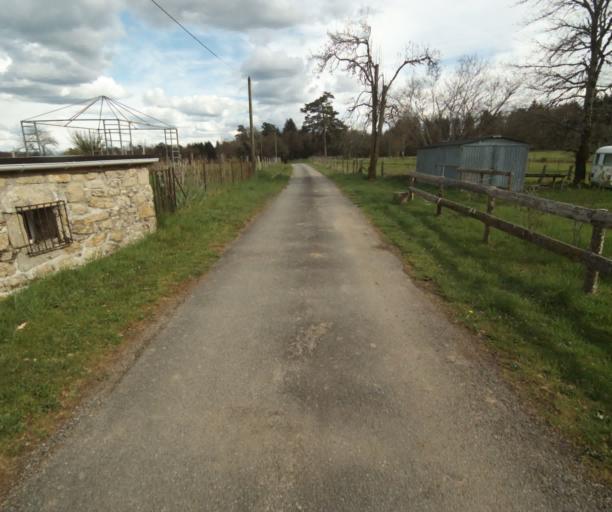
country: FR
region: Limousin
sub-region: Departement de la Correze
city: Argentat
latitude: 45.2118
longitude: 1.9576
